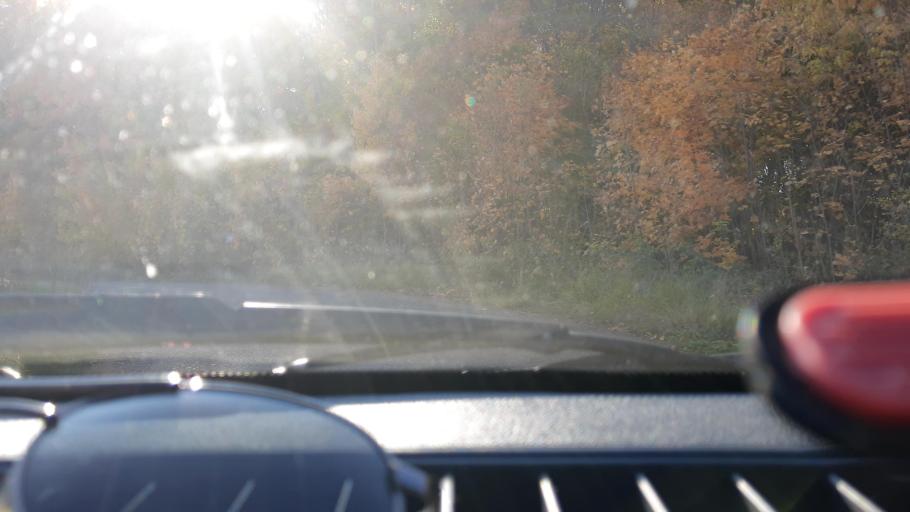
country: RU
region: Bashkortostan
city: Karmaskaly
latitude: 54.3775
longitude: 55.9107
